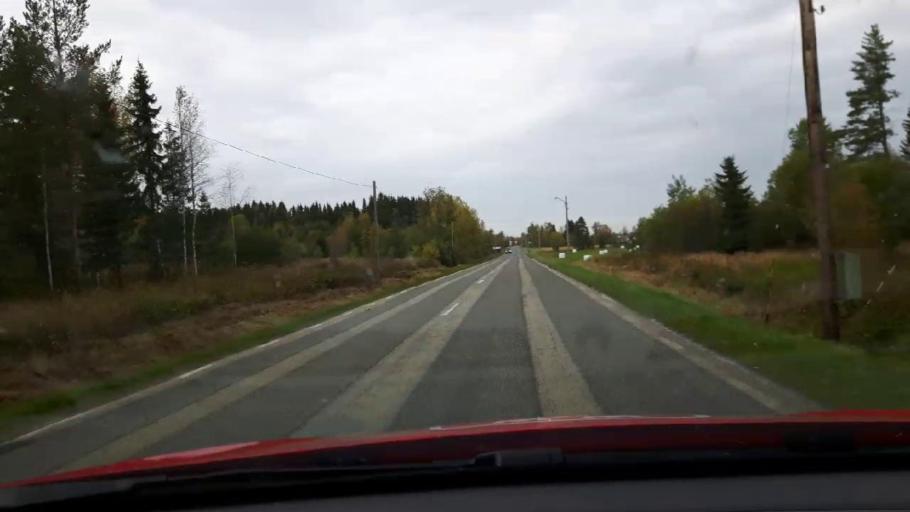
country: SE
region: Jaemtland
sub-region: Bergs Kommun
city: Hoverberg
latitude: 62.8262
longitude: 14.3908
